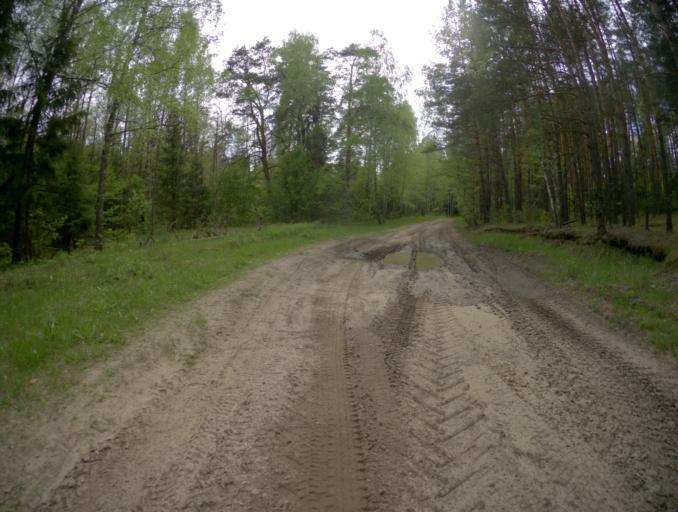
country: RU
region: Rjazan
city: Gus'-Zheleznyy
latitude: 55.0339
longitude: 41.1707
